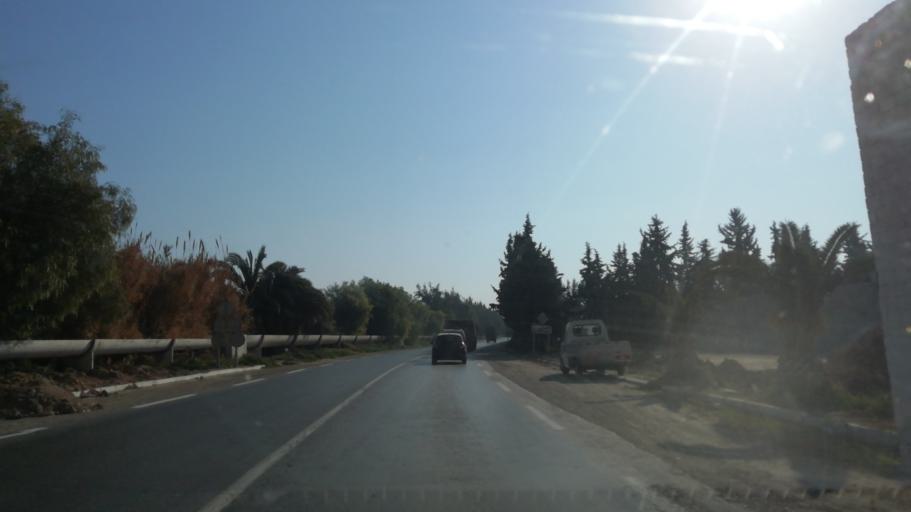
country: DZ
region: Relizane
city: Relizane
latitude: 35.7336
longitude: 0.4687
